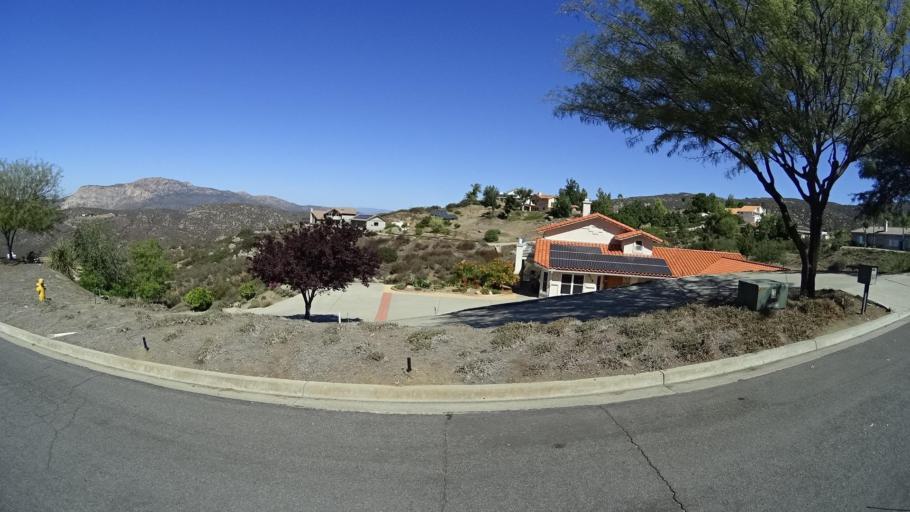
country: US
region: California
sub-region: San Diego County
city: Alpine
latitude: 32.8541
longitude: -116.7667
